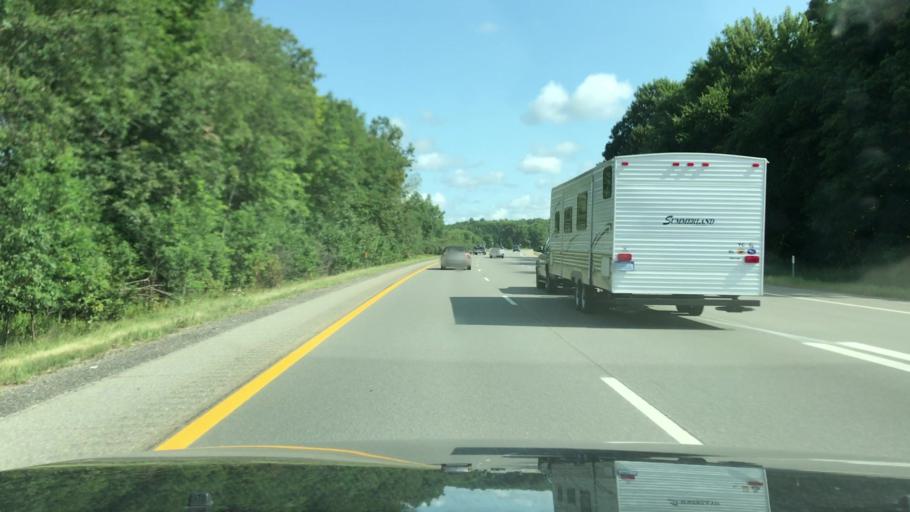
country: US
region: Michigan
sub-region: Kent County
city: Cedar Springs
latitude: 43.2987
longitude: -85.5421
